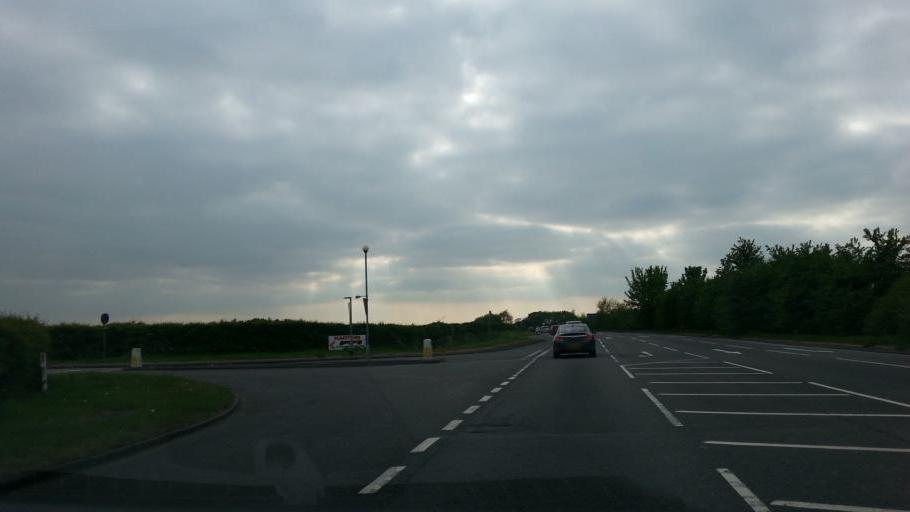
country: GB
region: England
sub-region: Lincolnshire
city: Navenby
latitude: 53.0686
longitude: -0.6350
